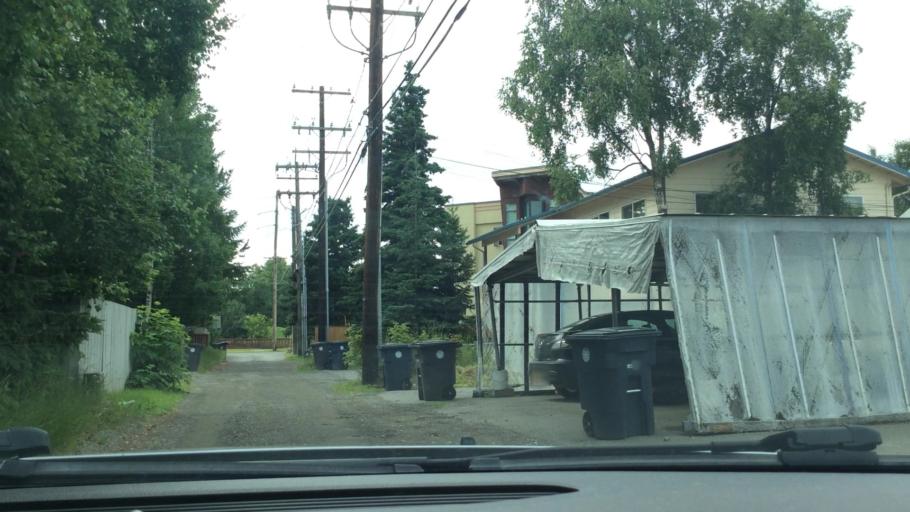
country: US
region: Alaska
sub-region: Anchorage Municipality
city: Anchorage
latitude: 61.2122
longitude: -149.8897
